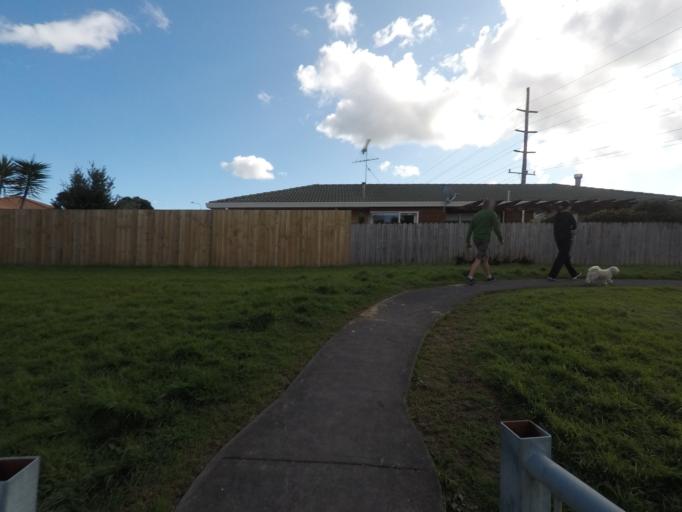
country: NZ
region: Auckland
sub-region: Auckland
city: Rothesay Bay
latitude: -36.7388
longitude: 174.6973
